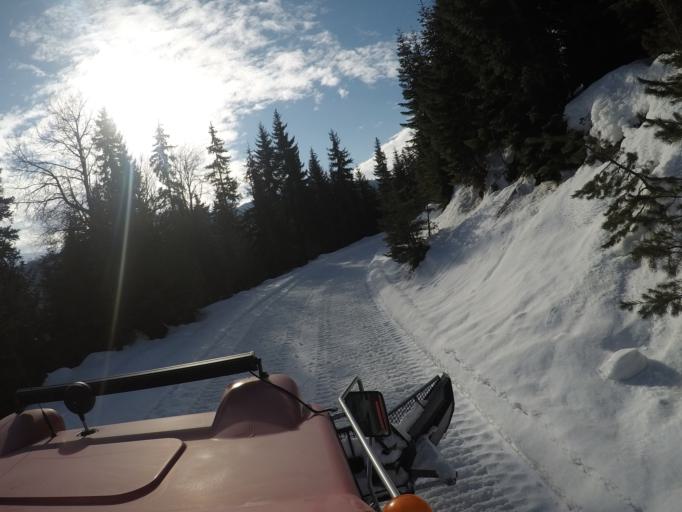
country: GE
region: Samtskhe-Javakheti
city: Adigeni
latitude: 41.6470
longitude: 42.5993
